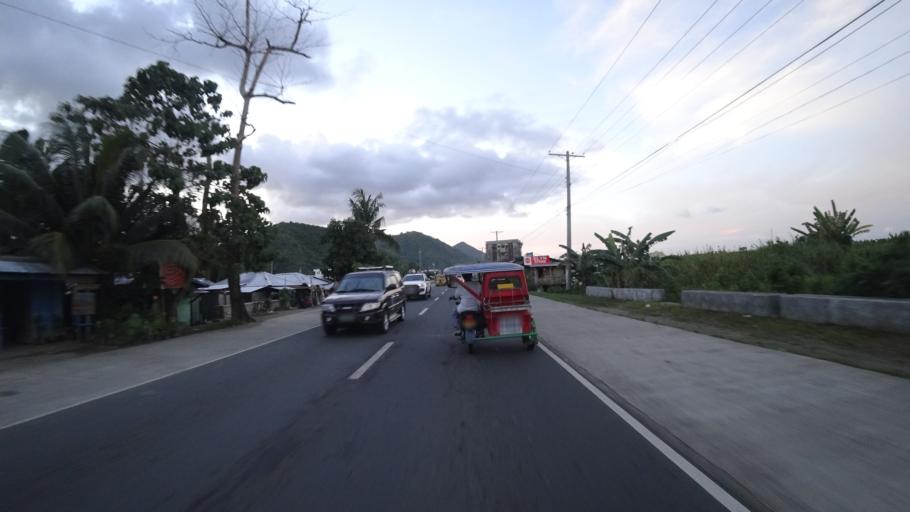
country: PH
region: Eastern Visayas
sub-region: Province of Leyte
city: Pawing
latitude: 11.1899
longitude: 124.9943
